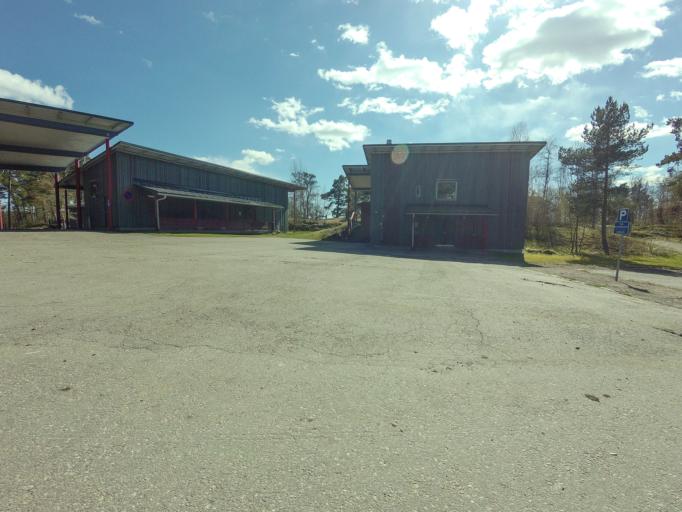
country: FI
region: Uusimaa
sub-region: Helsinki
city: Helsinki
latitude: 60.1610
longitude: 25.0452
